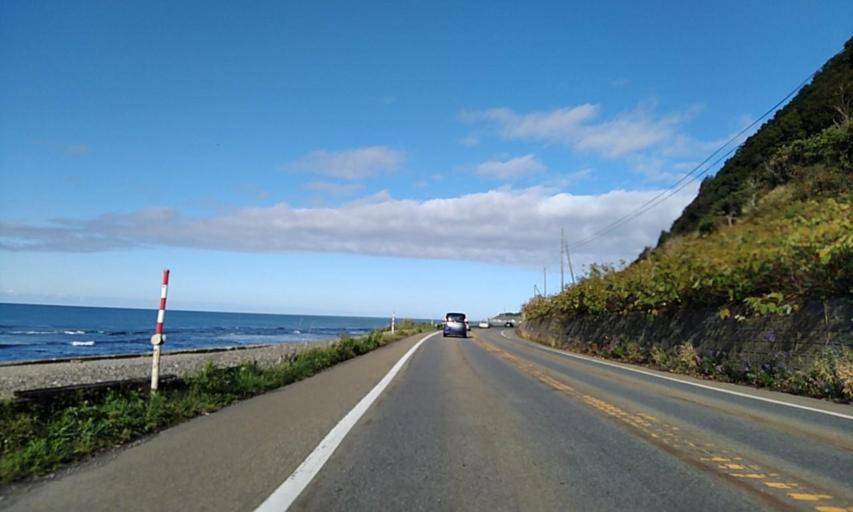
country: JP
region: Hokkaido
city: Shizunai-furukawacho
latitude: 42.2596
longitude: 142.5248
